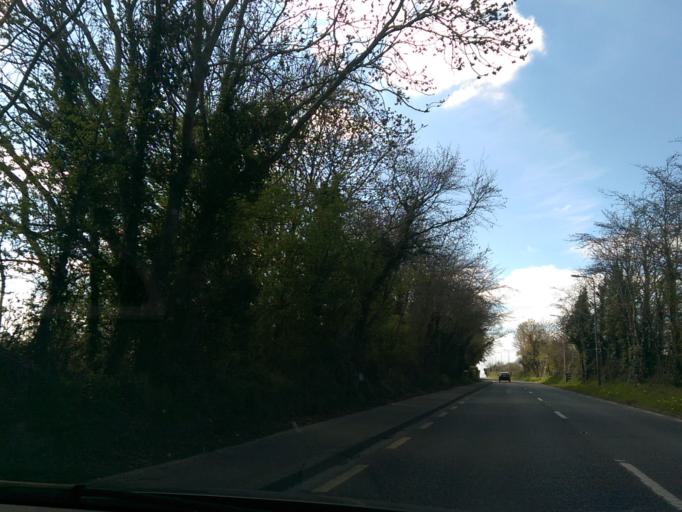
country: IE
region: Leinster
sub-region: Laois
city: Portlaoise
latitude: 53.0320
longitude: -7.2644
